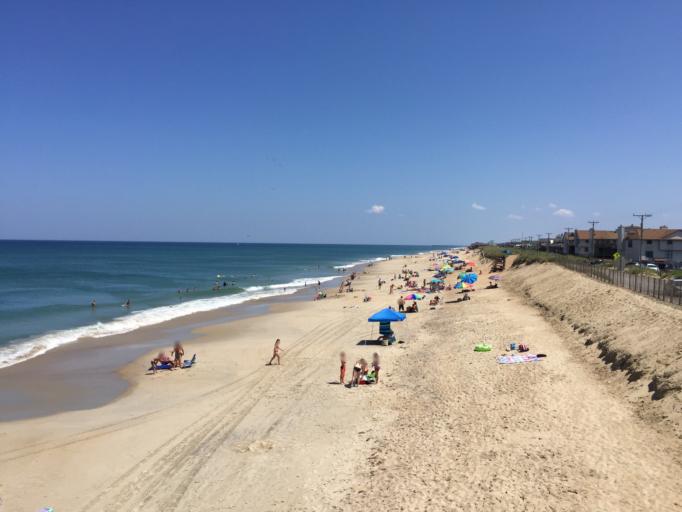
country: US
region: North Carolina
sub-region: Dare County
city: Kitty Hawk
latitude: 36.0674
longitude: -75.6906
